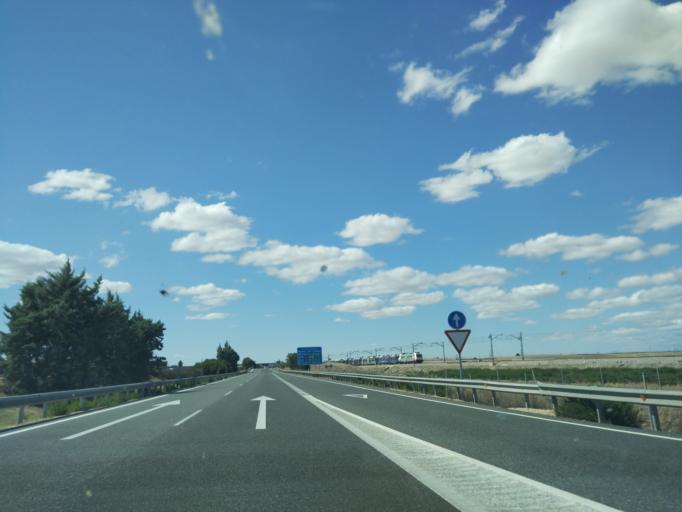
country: ES
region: Castille and Leon
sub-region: Provincia de Valladolid
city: Medina del Campo
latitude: 41.2784
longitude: -4.8908
